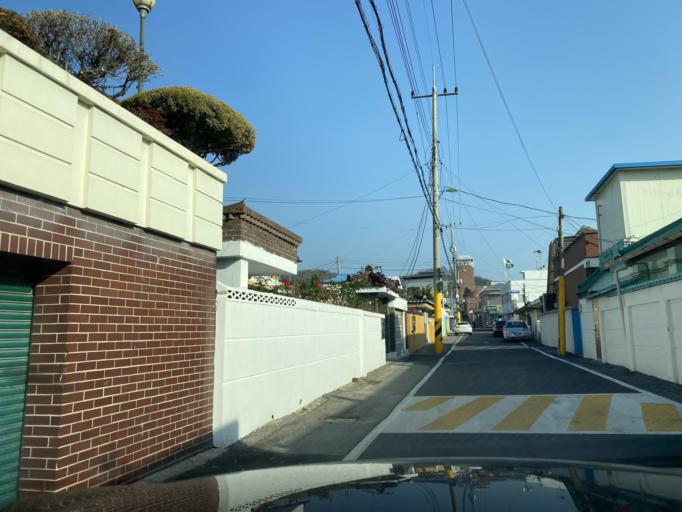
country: KR
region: Chungcheongnam-do
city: Yesan
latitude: 36.6775
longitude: 126.8459
